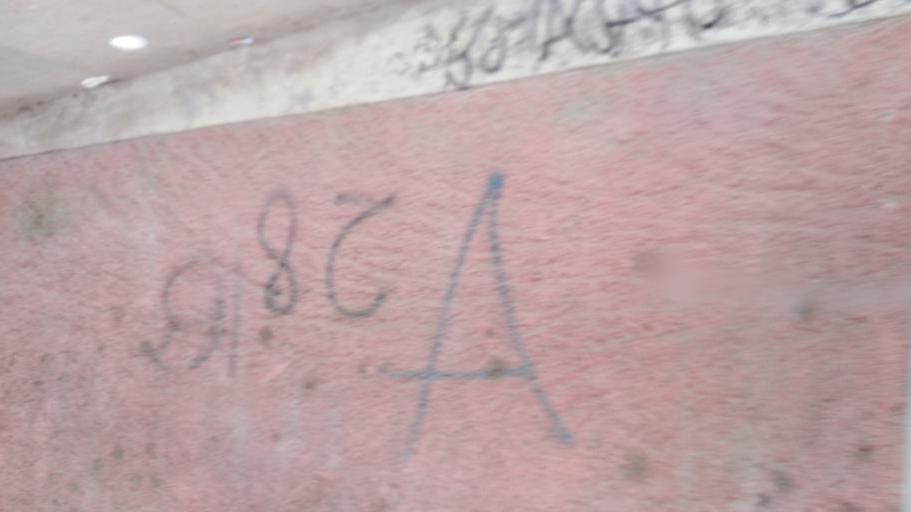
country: PE
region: Lima
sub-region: Lima
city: La Molina
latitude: -12.1424
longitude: -76.9410
